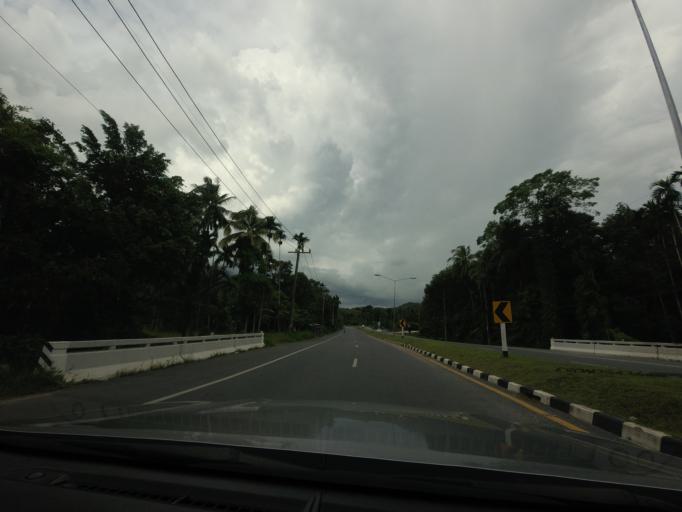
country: TH
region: Yala
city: Raman
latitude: 6.4737
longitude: 101.4112
